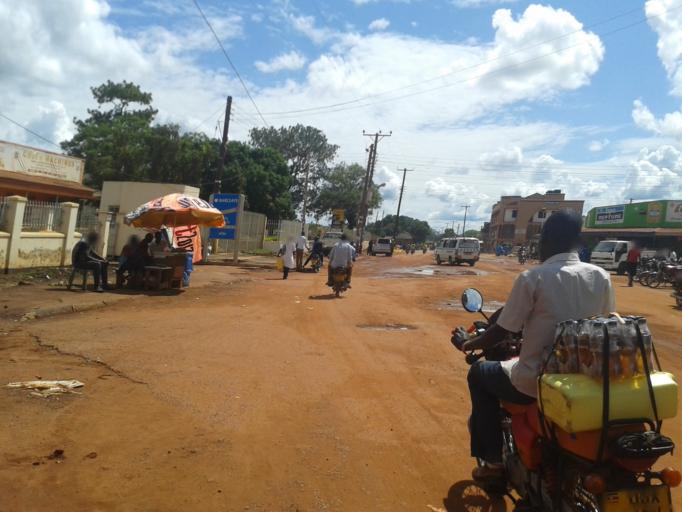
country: UG
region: Northern Region
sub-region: Gulu District
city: Gulu
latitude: 2.7699
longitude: 32.2996
